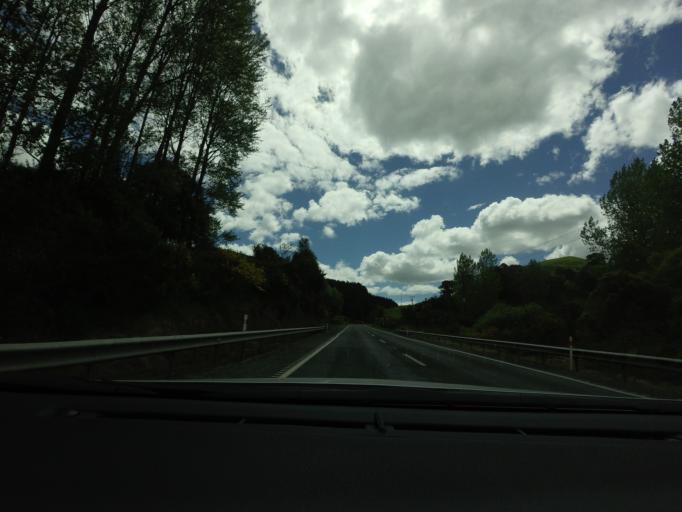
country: NZ
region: Bay of Plenty
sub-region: Rotorua District
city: Rotorua
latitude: -38.2964
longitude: 176.3589
